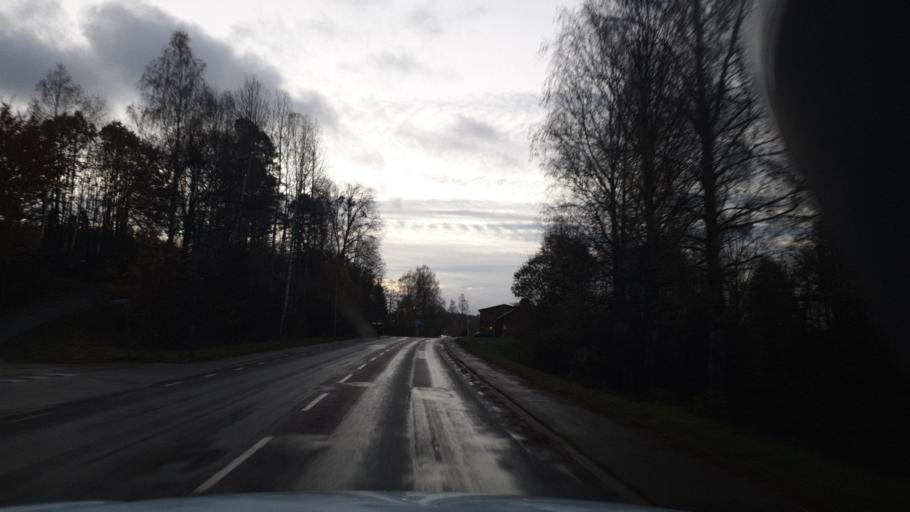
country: SE
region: Vaermland
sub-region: Arvika Kommun
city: Arvika
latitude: 59.6279
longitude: 12.8277
